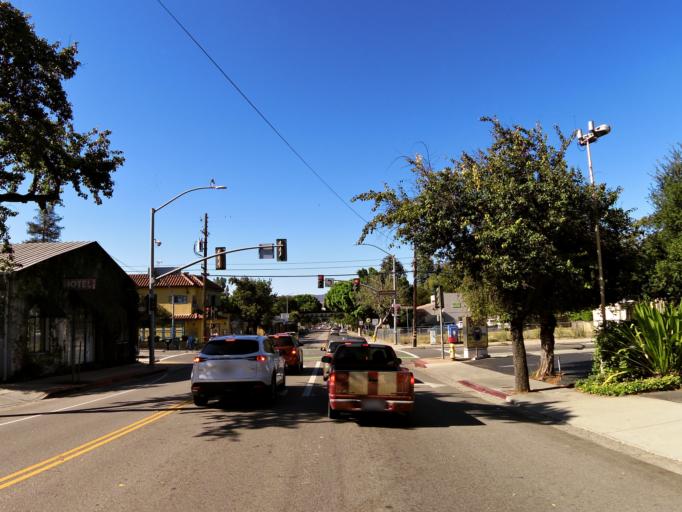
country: US
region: California
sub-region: San Luis Obispo County
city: San Luis Obispo
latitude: 35.2863
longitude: -120.6542
